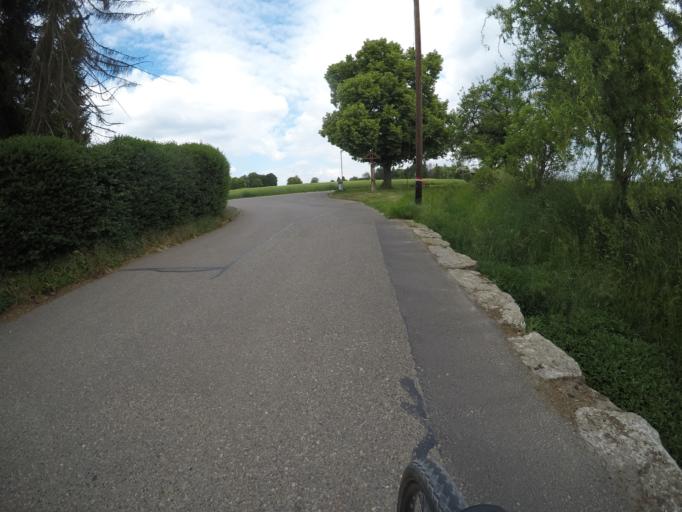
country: DE
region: Baden-Wuerttemberg
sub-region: Regierungsbezirk Stuttgart
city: Kongen
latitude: 48.6904
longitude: 9.3712
